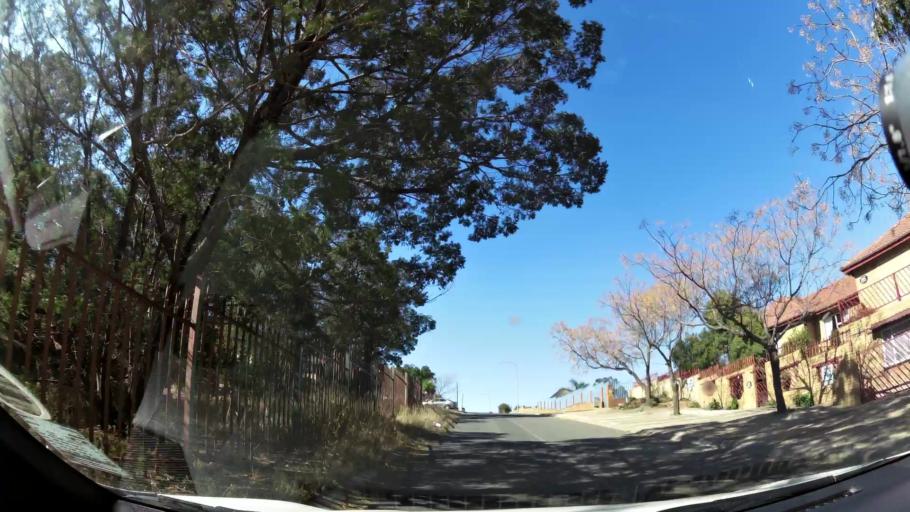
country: ZA
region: Gauteng
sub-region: City of Johannesburg Metropolitan Municipality
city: Johannesburg
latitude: -26.2610
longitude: 28.0028
